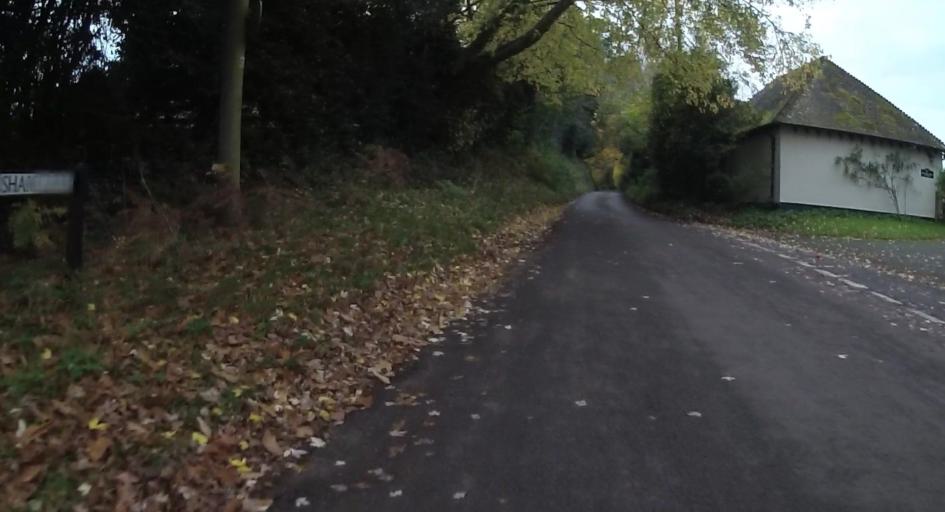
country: GB
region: England
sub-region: Hampshire
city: Lindford
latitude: 51.1335
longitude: -0.8236
